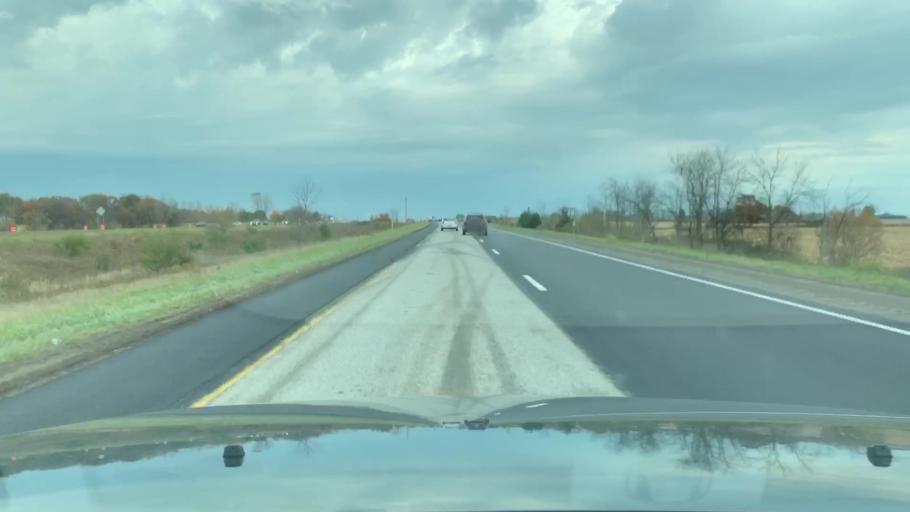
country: US
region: Michigan
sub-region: Ottawa County
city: Zeeland
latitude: 42.8211
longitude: -85.9385
